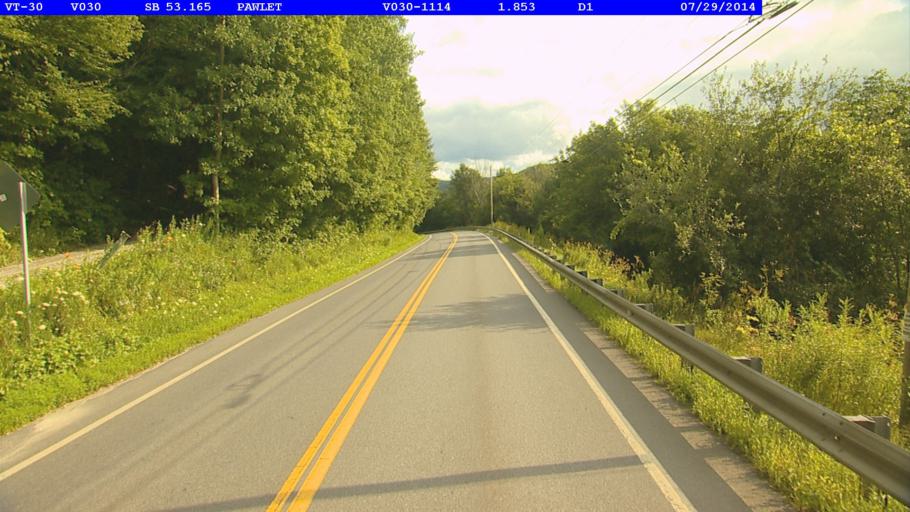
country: US
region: New York
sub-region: Washington County
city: Granville
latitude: 43.3367
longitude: -73.1768
